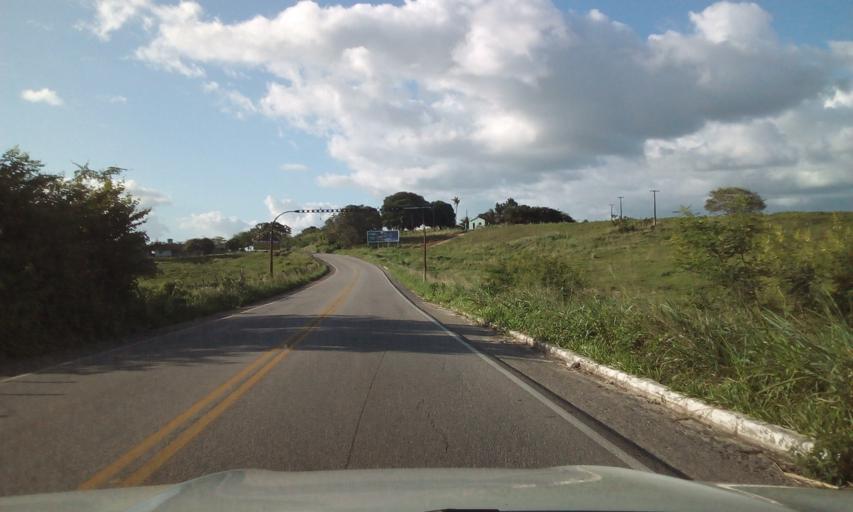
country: BR
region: Paraiba
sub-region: Pilar
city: Pilar
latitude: -7.1905
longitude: -35.2312
